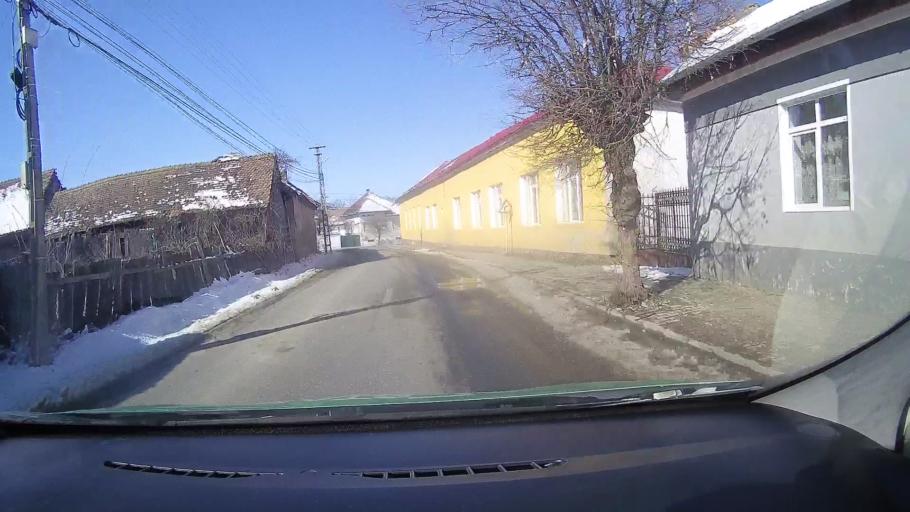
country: RO
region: Brasov
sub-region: Comuna Harseni
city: Harseni
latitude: 45.7886
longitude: 24.9981
